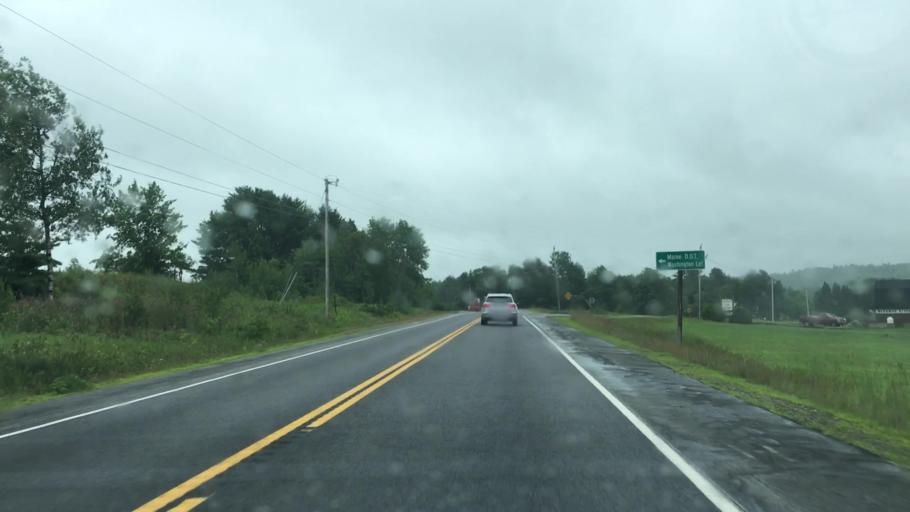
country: US
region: Maine
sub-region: Knox County
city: Washington
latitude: 44.2334
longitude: -69.3527
